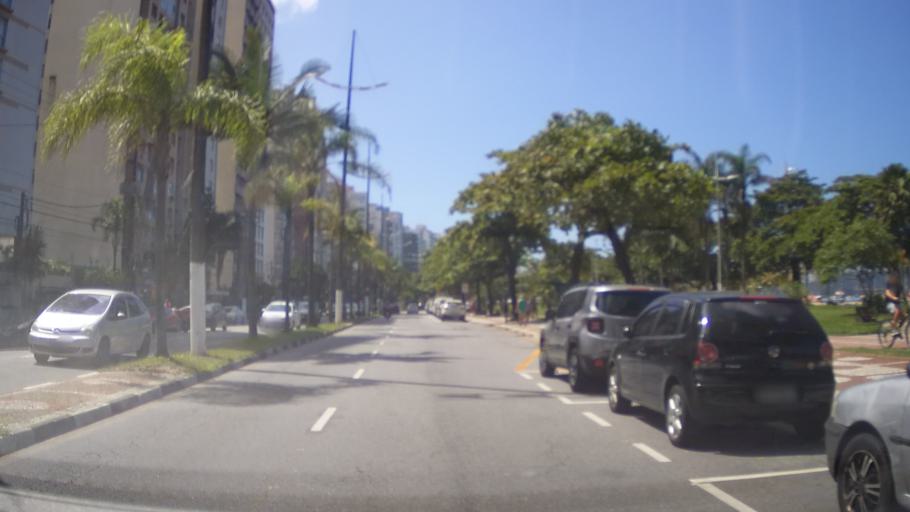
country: BR
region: Sao Paulo
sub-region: Santos
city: Santos
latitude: -23.9716
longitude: -46.3269
